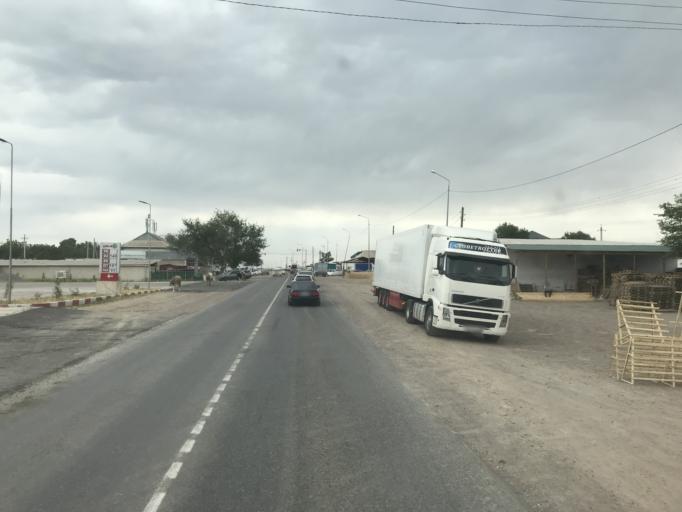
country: KZ
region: Ongtustik Qazaqstan
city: Saryaghash
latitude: 41.4317
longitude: 69.1092
